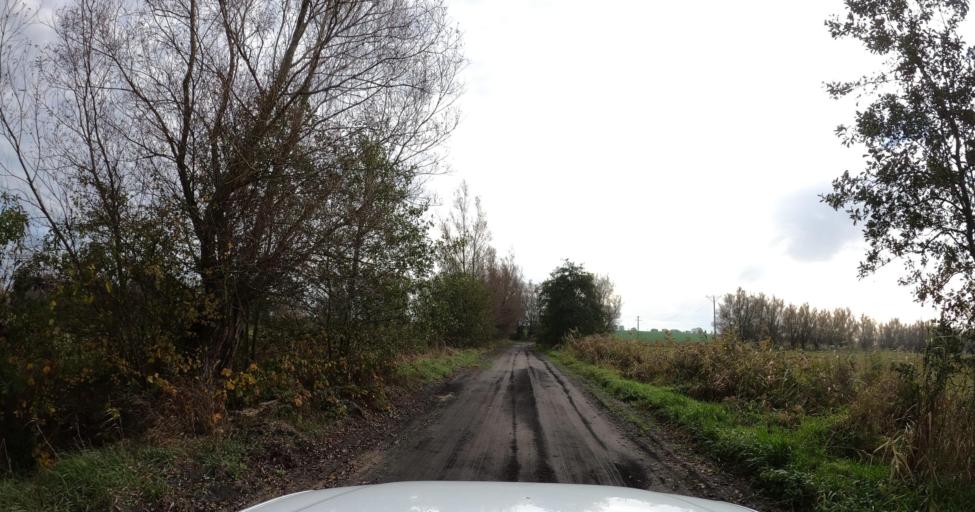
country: PL
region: West Pomeranian Voivodeship
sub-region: Powiat kamienski
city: Kamien Pomorski
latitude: 53.9855
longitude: 14.8512
